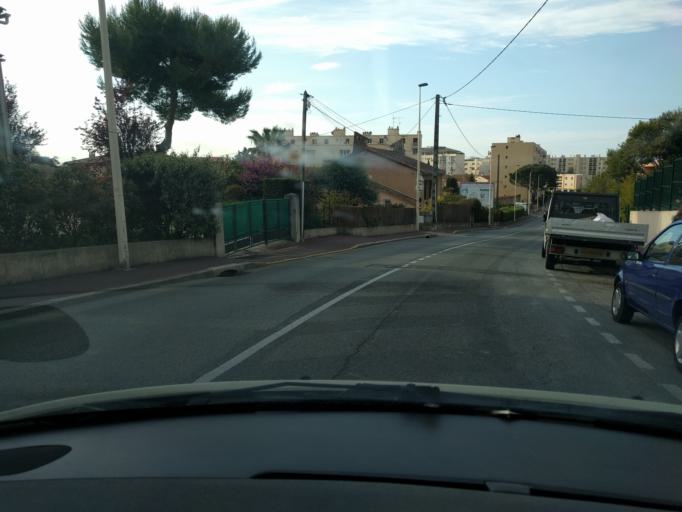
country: FR
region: Provence-Alpes-Cote d'Azur
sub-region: Departement des Alpes-Maritimes
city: Cannes
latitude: 43.5561
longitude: 6.9733
